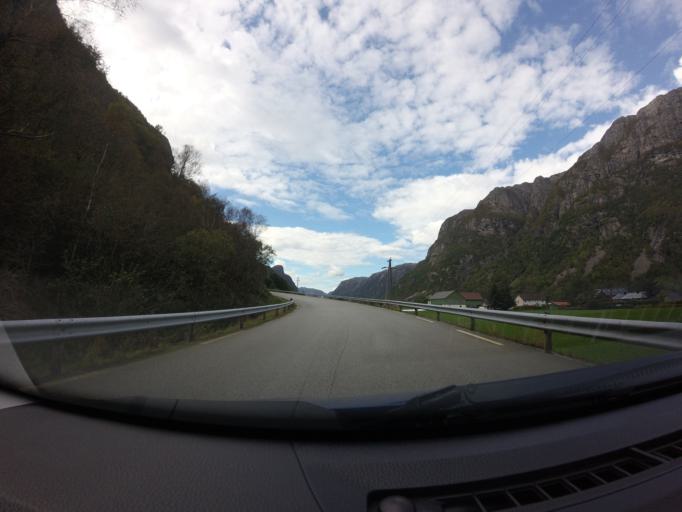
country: NO
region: Rogaland
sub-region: Forsand
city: Forsand
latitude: 58.8416
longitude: 6.3110
